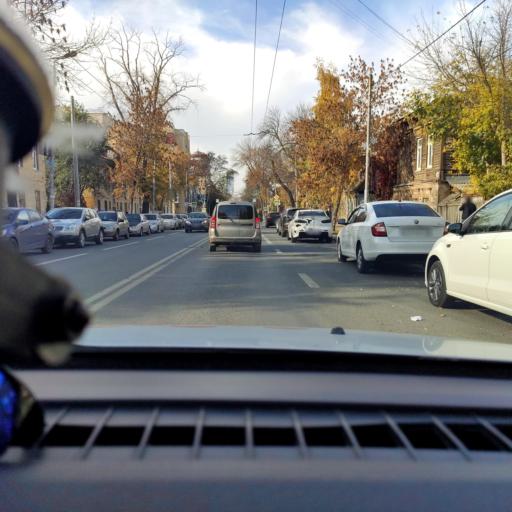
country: RU
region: Samara
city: Samara
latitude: 53.1974
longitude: 50.1155
